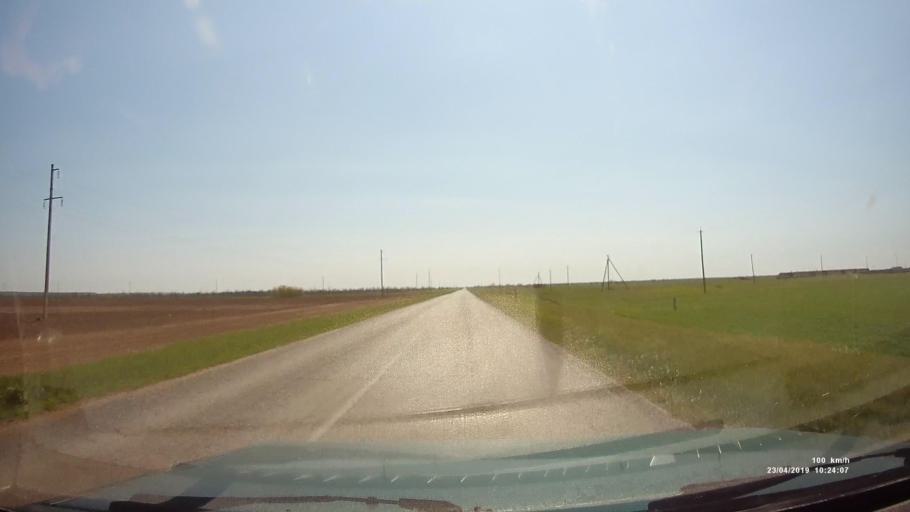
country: RU
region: Rostov
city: Sovetskoye
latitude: 46.6416
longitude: 42.4362
